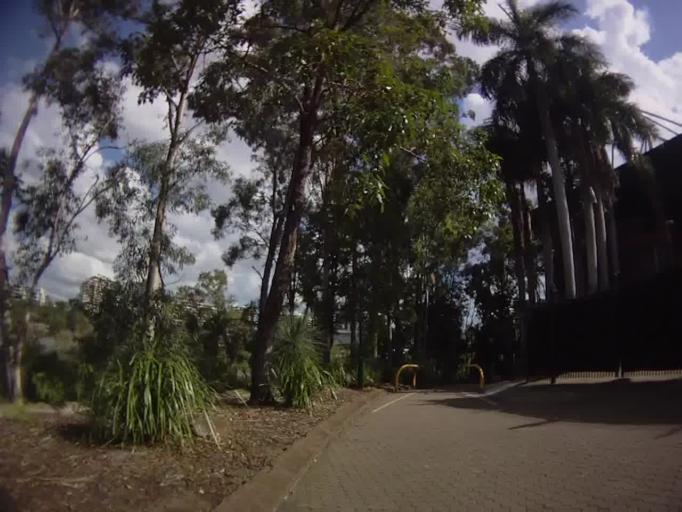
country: AU
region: Queensland
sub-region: Brisbane
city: South Brisbane
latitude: -27.4790
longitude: 153.0305
